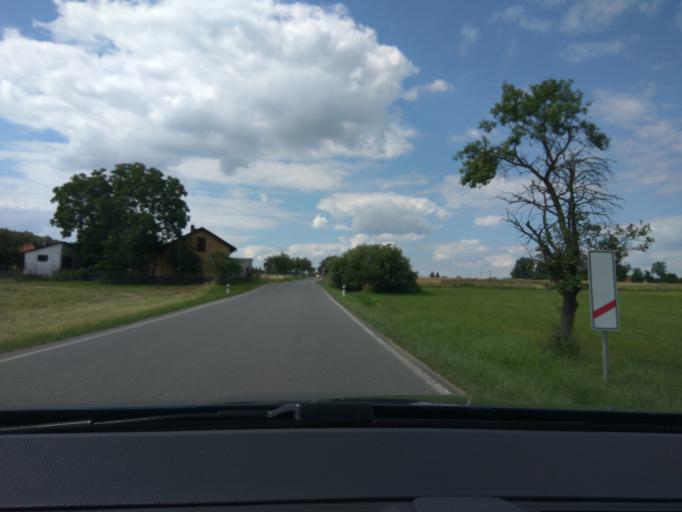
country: CZ
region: Jihocesky
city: Milevsko
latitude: 49.4088
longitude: 14.3607
